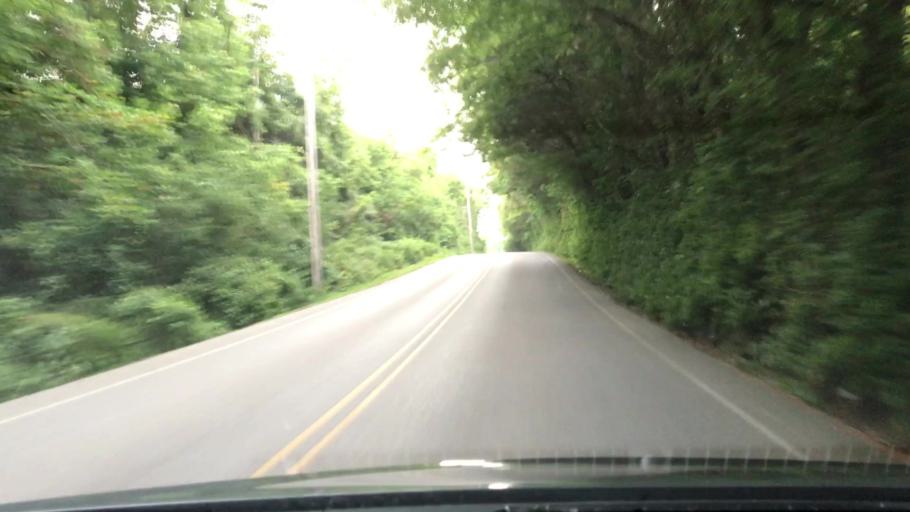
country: US
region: Tennessee
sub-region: Williamson County
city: Nolensville
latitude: 35.9685
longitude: -86.6221
